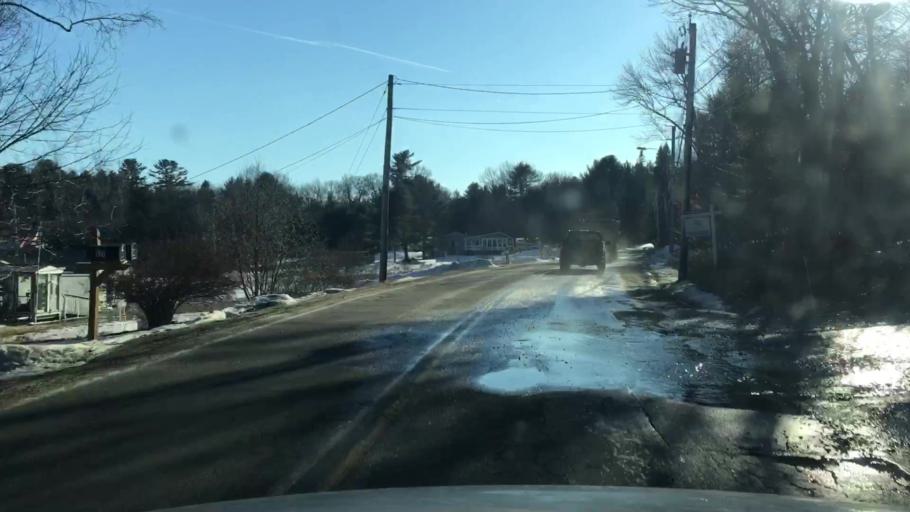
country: US
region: Maine
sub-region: Cumberland County
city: Westbrook
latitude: 43.7161
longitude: -70.3586
